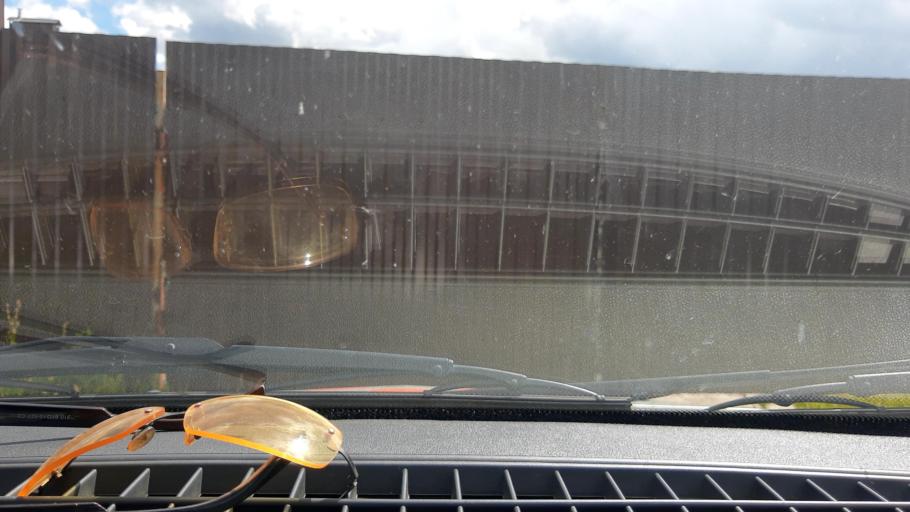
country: RU
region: Bashkortostan
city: Ufa
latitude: 54.7052
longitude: 56.1058
